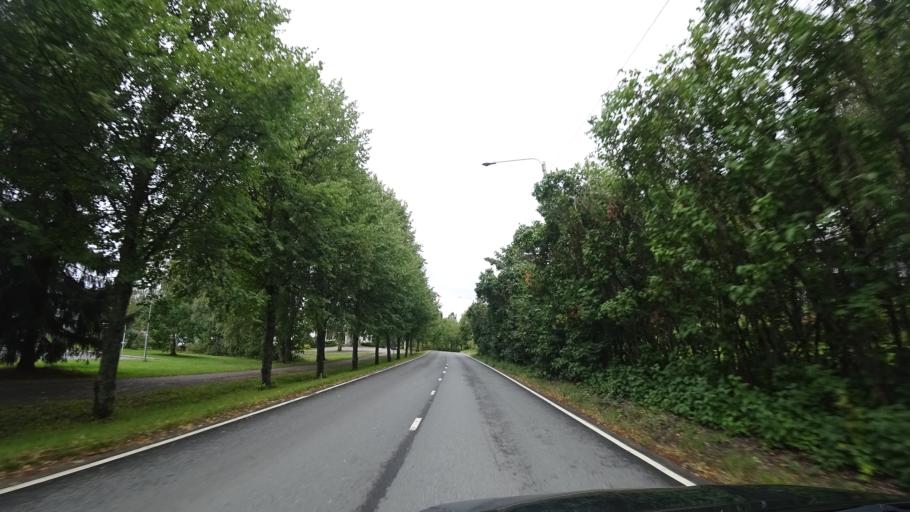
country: FI
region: Haeme
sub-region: Haemeenlinna
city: Lammi
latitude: 61.0834
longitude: 25.0085
